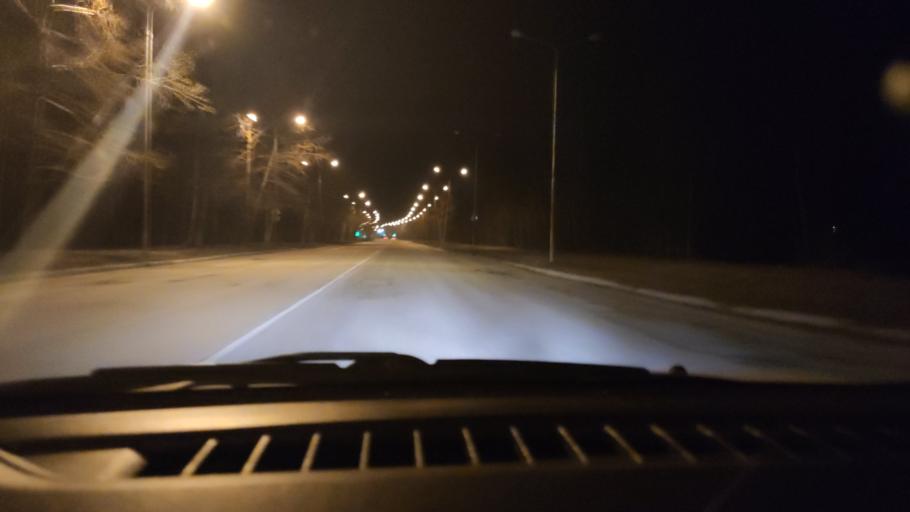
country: RU
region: Perm
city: Perm
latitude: 58.0860
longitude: 56.3793
